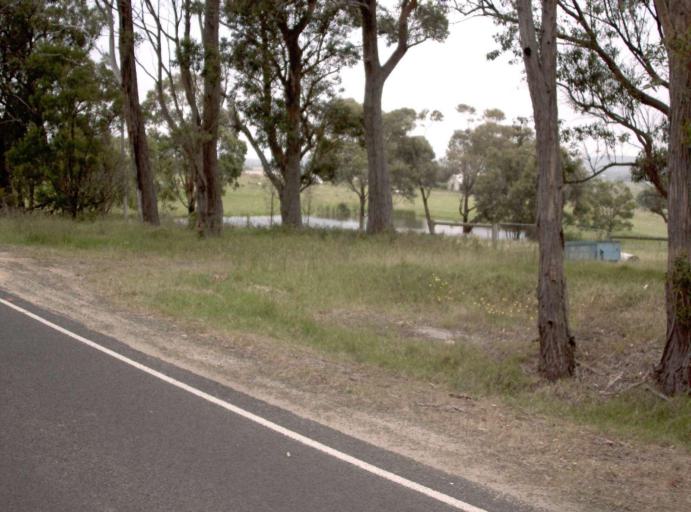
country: AU
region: Victoria
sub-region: Latrobe
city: Traralgon
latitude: -38.4753
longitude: 146.7166
